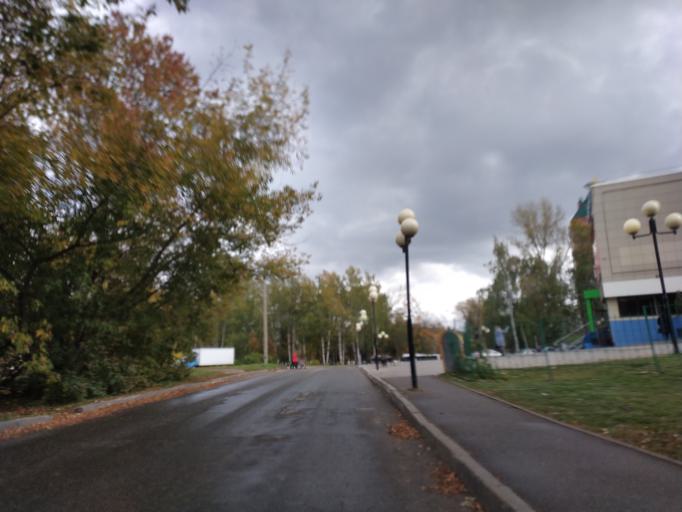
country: RU
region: Chuvashia
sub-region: Cheboksarskiy Rayon
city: Cheboksary
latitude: 56.1464
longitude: 47.2154
